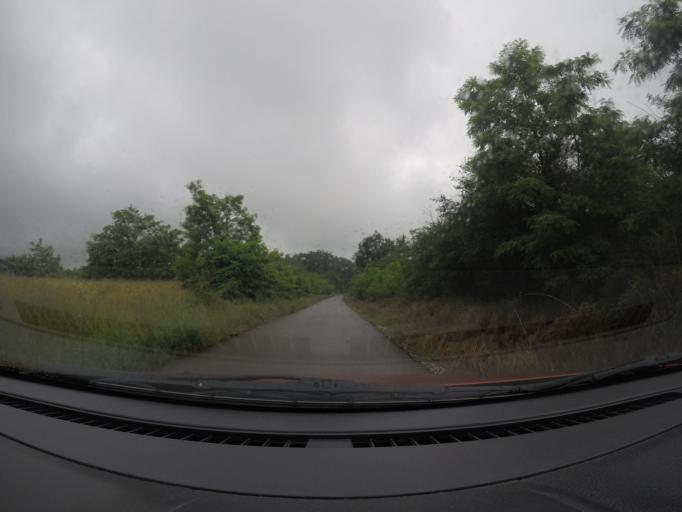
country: RS
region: Central Serbia
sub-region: Belgrade
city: Sopot
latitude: 44.5549
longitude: 20.5285
